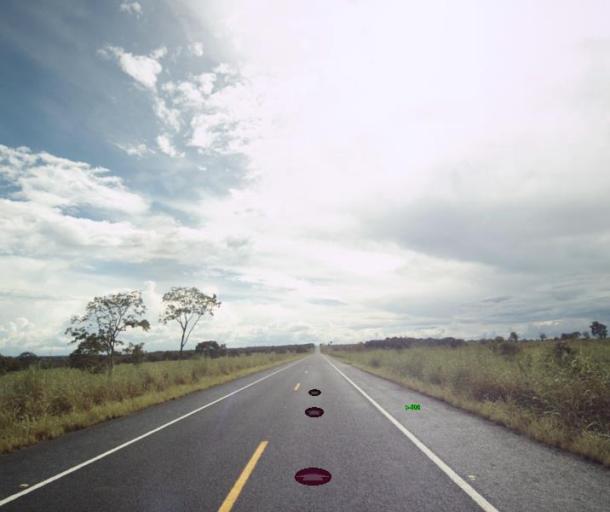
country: BR
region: Goias
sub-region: Sao Miguel Do Araguaia
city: Sao Miguel do Araguaia
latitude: -13.2938
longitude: -50.3828
